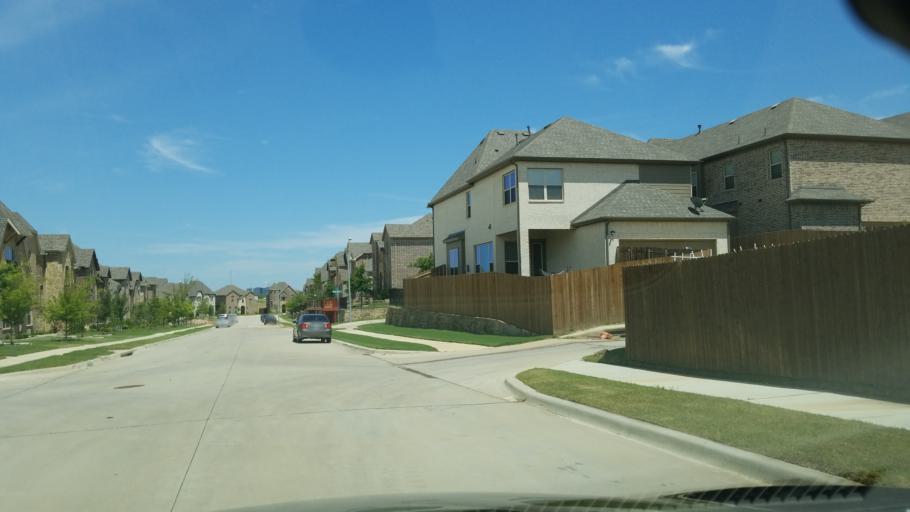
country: US
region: Texas
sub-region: Dallas County
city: Coppell
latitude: 32.8801
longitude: -96.9977
